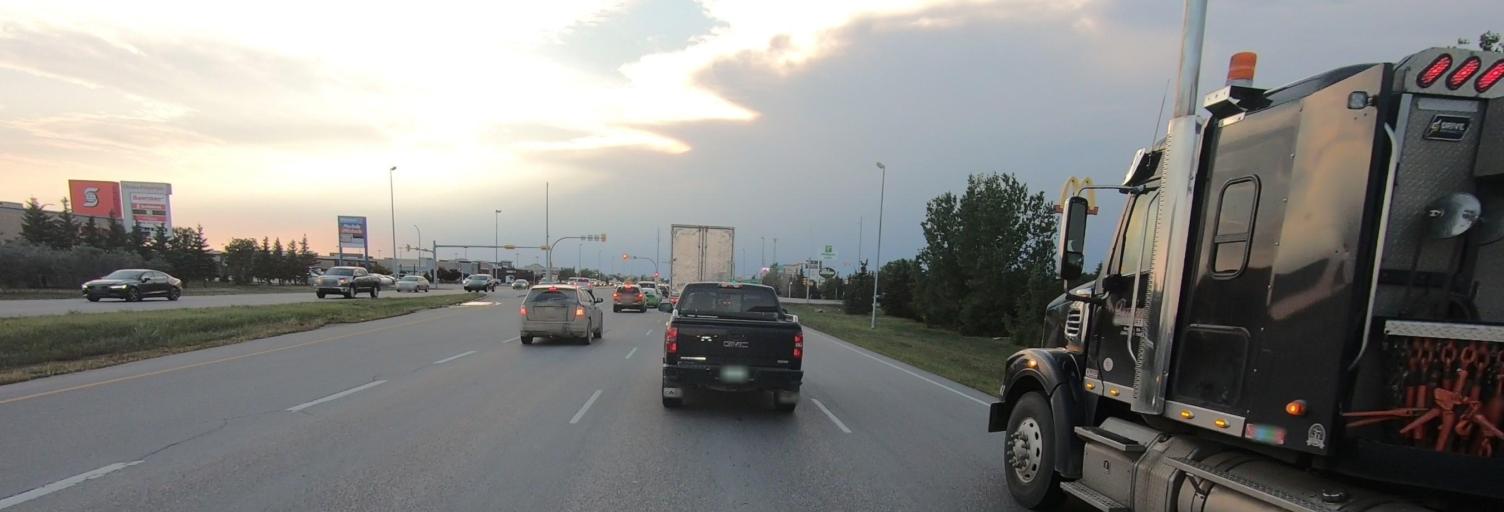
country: CA
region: Saskatchewan
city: Regina
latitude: 50.4477
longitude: -104.5310
